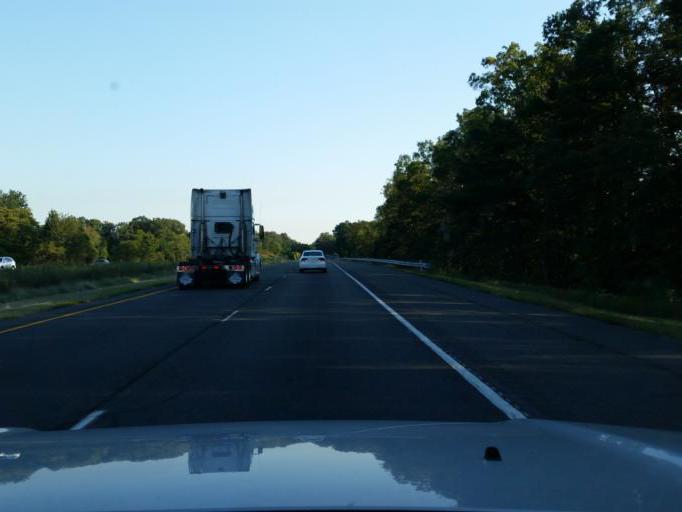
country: US
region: New Jersey
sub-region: Gloucester County
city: Newfield
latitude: 39.5594
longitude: -75.0596
